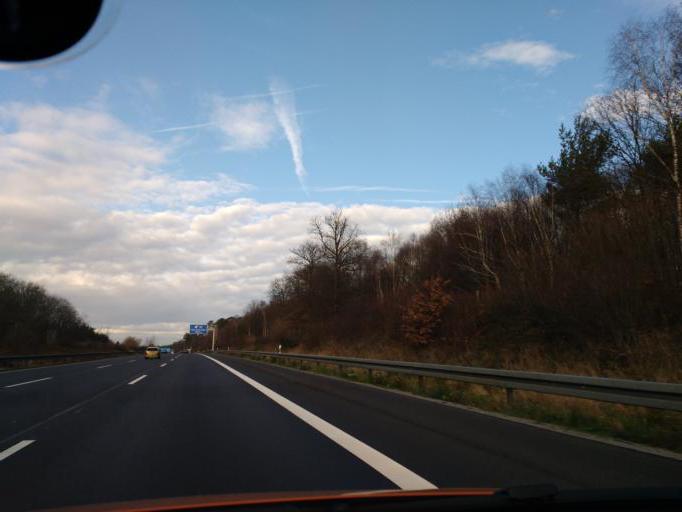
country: DE
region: Lower Saxony
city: Mariental
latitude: 52.2541
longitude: 10.9971
